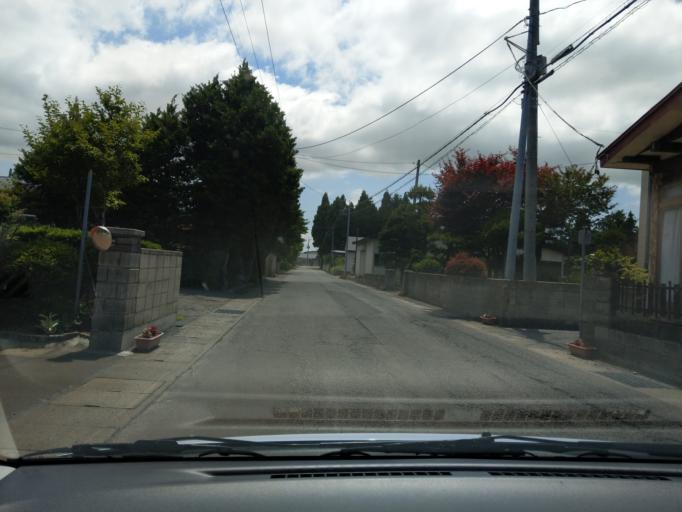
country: JP
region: Aomori
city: Kuroishi
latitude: 40.6788
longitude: 140.5597
